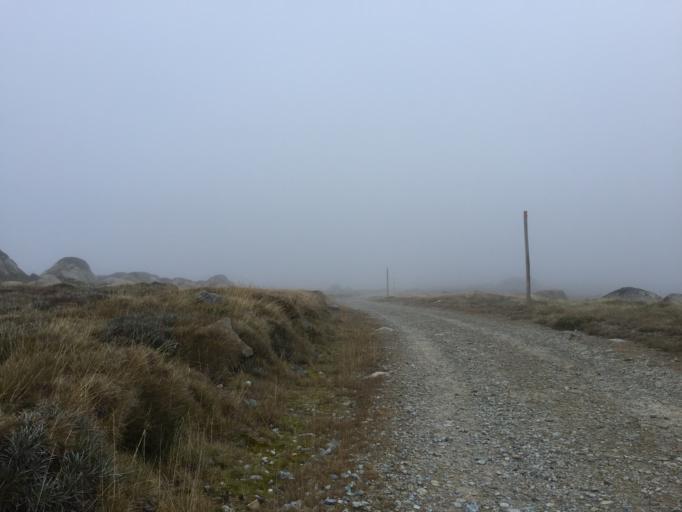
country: AU
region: New South Wales
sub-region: Snowy River
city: Jindabyne
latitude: -36.4535
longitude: 148.2873
